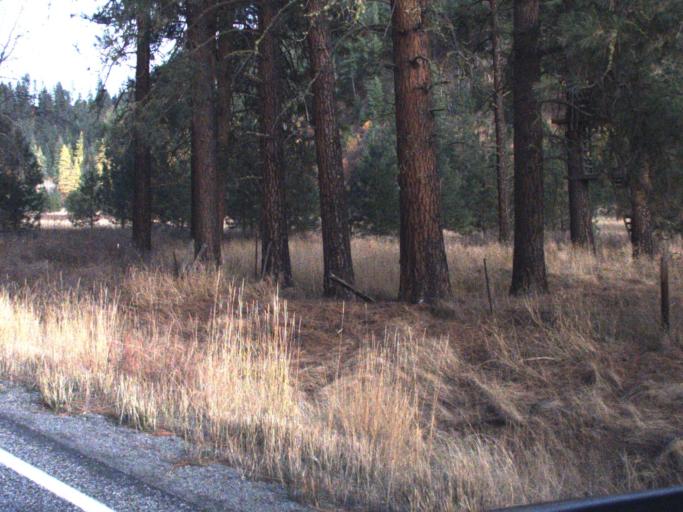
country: US
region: Washington
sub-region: Stevens County
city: Kettle Falls
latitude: 48.8265
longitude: -117.9120
